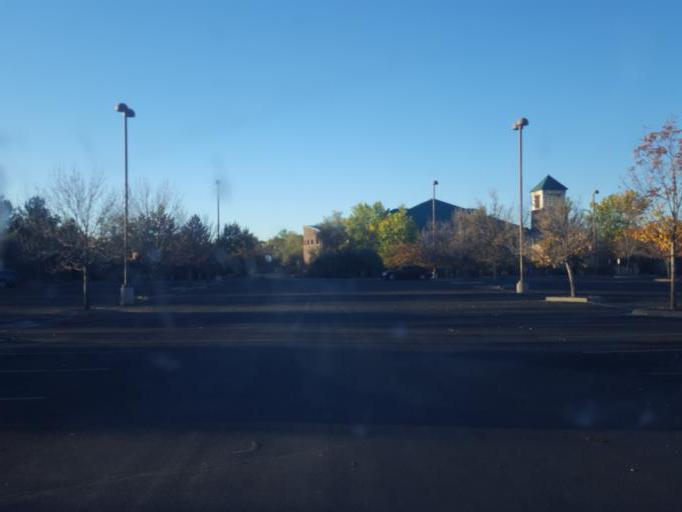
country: US
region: New Mexico
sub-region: Bernalillo County
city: Albuquerque
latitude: 35.0945
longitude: -106.6785
